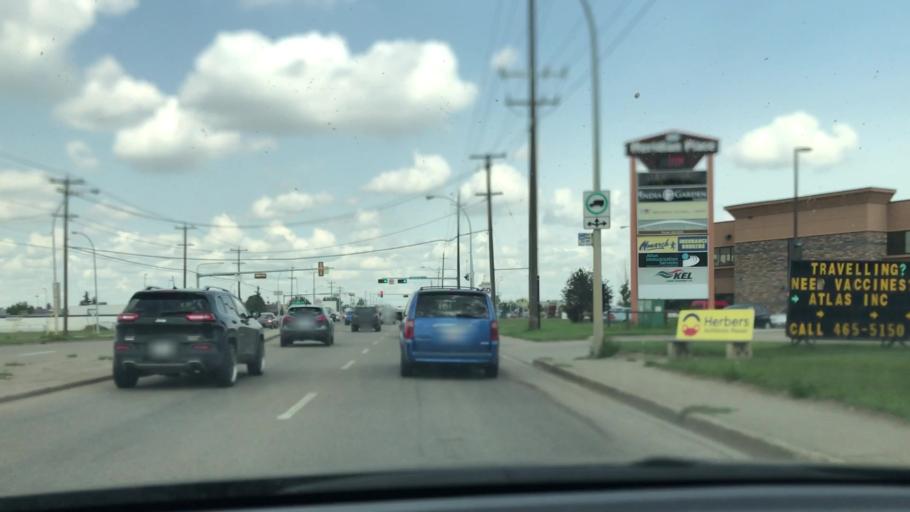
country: CA
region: Alberta
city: Edmonton
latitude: 53.5129
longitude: -113.4183
